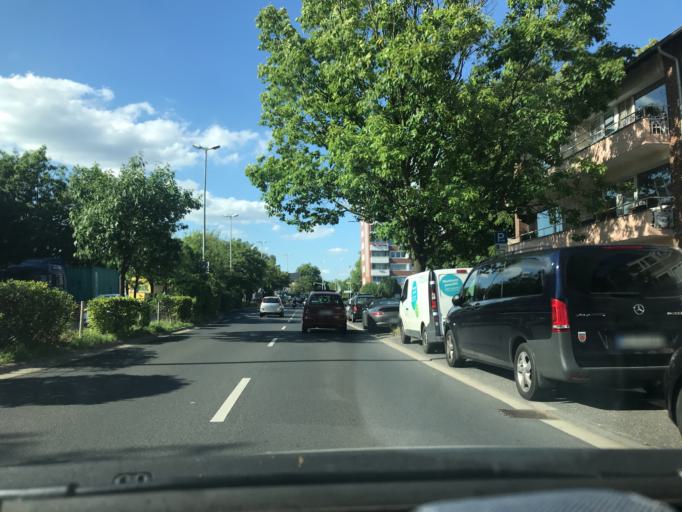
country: DE
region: North Rhine-Westphalia
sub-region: Regierungsbezirk Dusseldorf
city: Neuss
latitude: 51.1660
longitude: 6.6841
